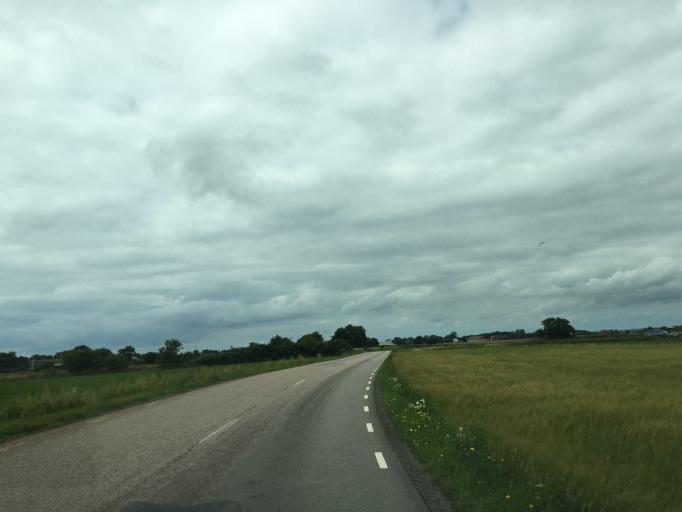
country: SE
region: Skane
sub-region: Angelholms Kommun
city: Vejbystrand
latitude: 56.3162
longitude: 12.7847
